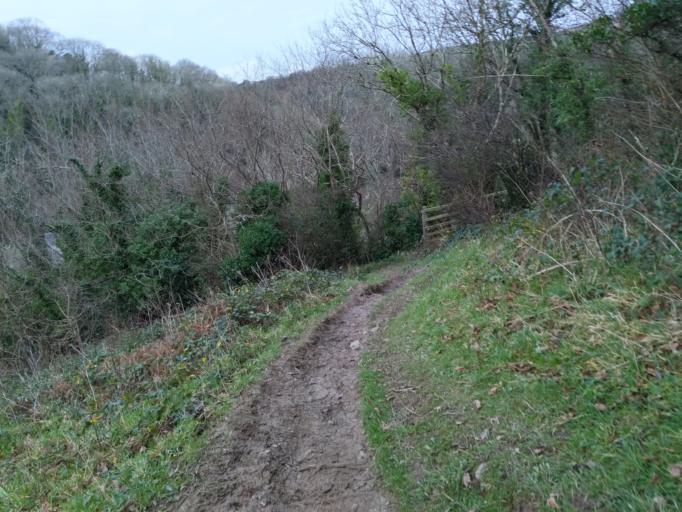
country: GB
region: England
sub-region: Cornwall
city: Fowey
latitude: 50.3366
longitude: -4.6113
